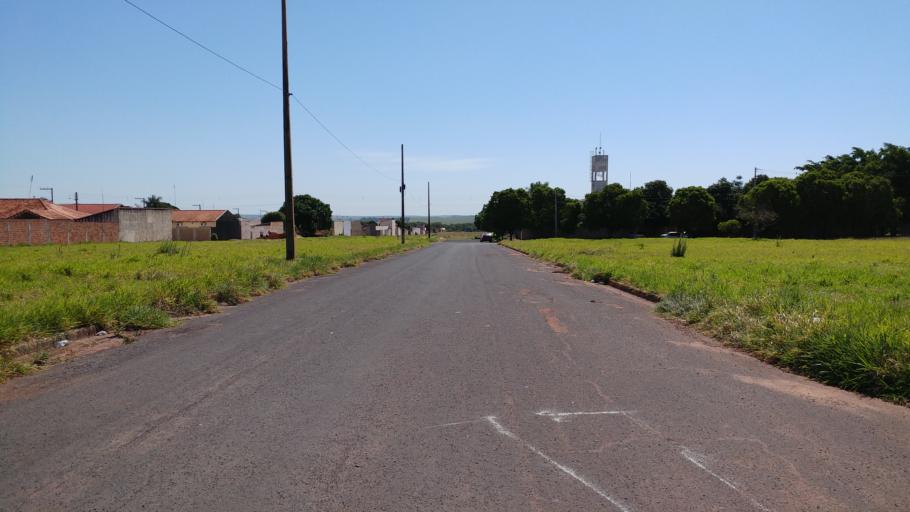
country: BR
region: Sao Paulo
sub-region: Paraguacu Paulista
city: Paraguacu Paulista
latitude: -22.4125
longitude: -50.5869
